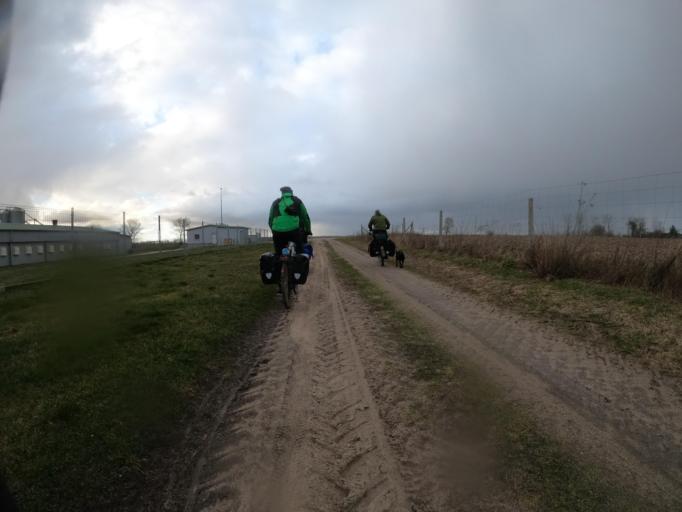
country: PL
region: Greater Poland Voivodeship
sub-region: Powiat zlotowski
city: Sypniewo
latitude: 53.4619
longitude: 16.5883
